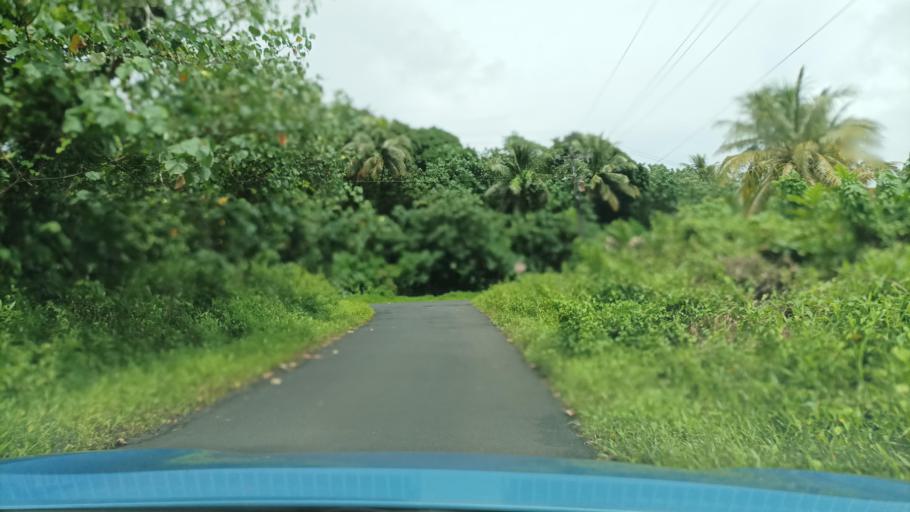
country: FM
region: Pohnpei
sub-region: Madolenihm Municipality
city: Madolenihm Municipality Government
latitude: 6.8978
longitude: 158.3162
